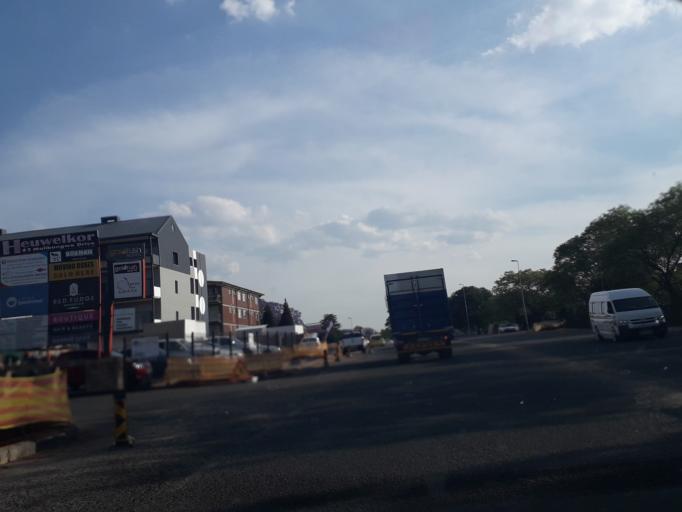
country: ZA
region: Gauteng
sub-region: City of Johannesburg Metropolitan Municipality
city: Johannesburg
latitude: -26.1219
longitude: 27.9886
